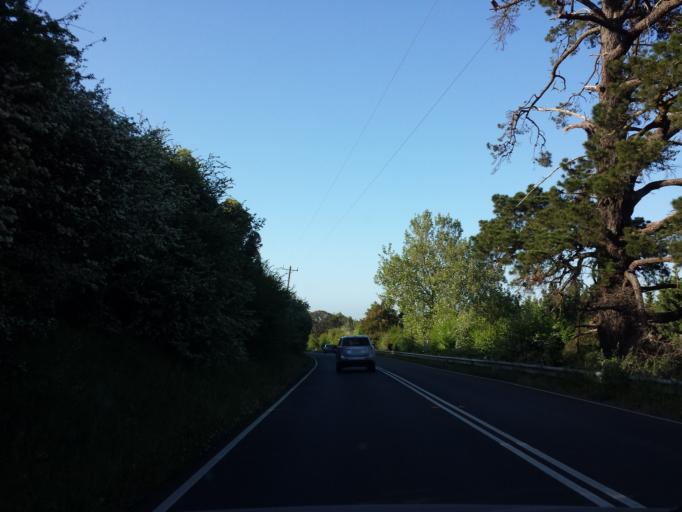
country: AU
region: Victoria
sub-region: Casey
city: Berwick
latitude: -38.0121
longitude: 145.3440
